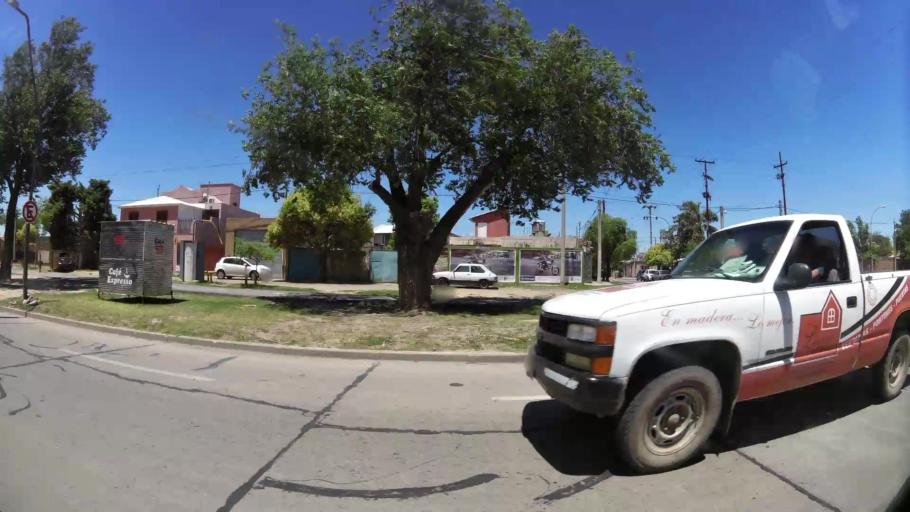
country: AR
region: Cordoba
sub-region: Departamento de Capital
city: Cordoba
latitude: -31.3778
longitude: -64.1349
